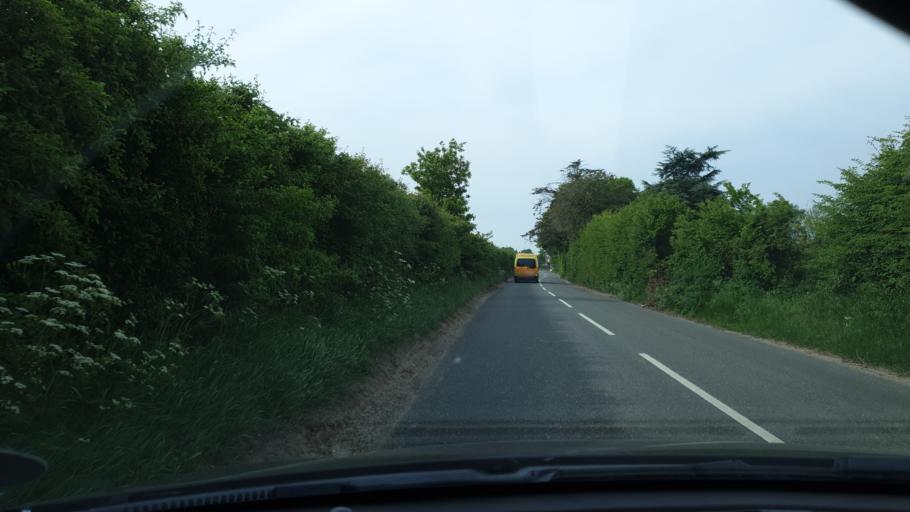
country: GB
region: England
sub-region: Essex
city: Great Bentley
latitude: 51.8609
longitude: 1.0658
